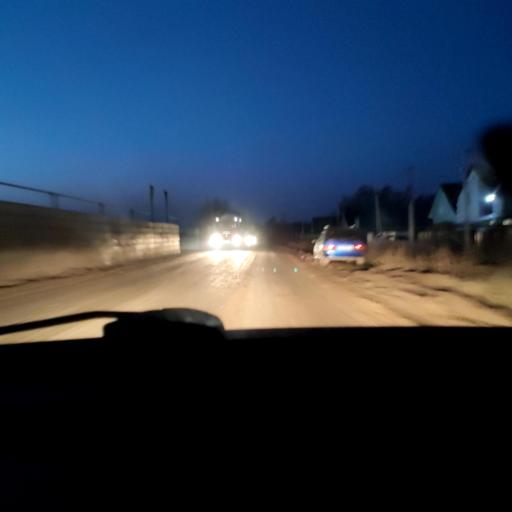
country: RU
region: Bashkortostan
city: Kabakovo
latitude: 54.6974
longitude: 56.1314
